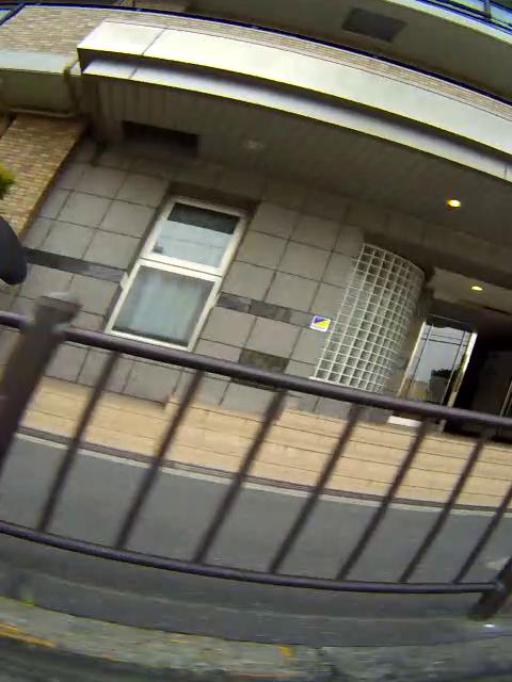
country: JP
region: Osaka
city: Mino
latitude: 34.8065
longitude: 135.4718
